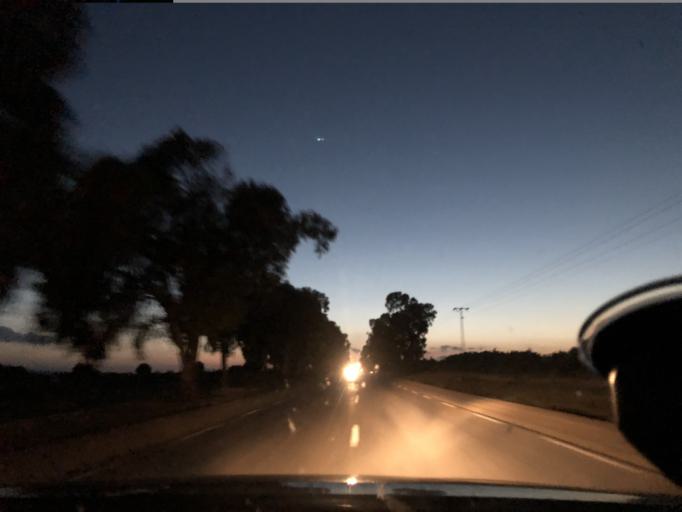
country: TN
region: Al Qasrayn
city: Kasserine
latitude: 35.2645
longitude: 9.0551
